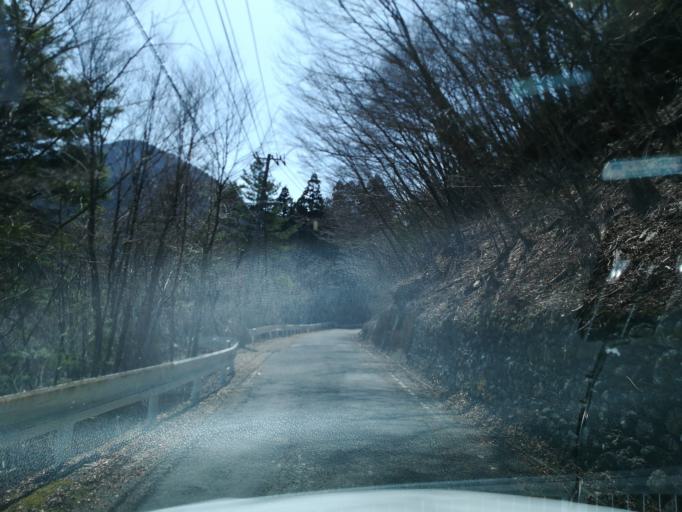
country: JP
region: Tokushima
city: Wakimachi
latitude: 33.8562
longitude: 134.0484
